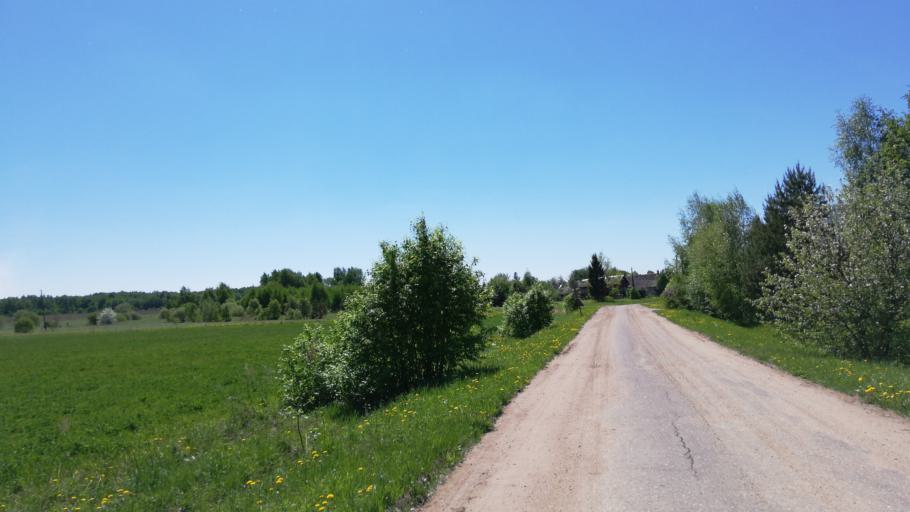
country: RU
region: Ivanovo
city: Pistsovo
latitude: 57.1192
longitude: 40.5979
